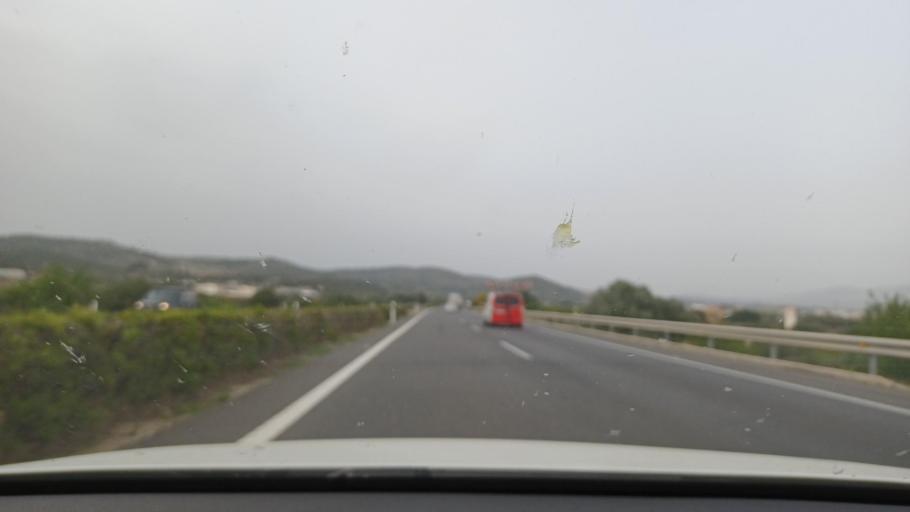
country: ES
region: Valencia
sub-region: Provincia de Castello
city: Torreblanca
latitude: 40.1994
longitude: 0.1750
